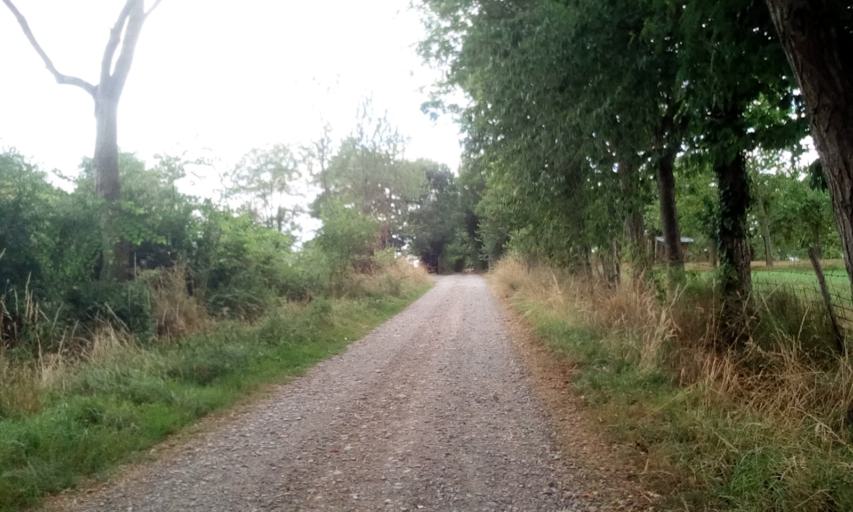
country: FR
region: Lower Normandy
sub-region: Departement du Calvados
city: Troarn
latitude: 49.1600
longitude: -0.1750
